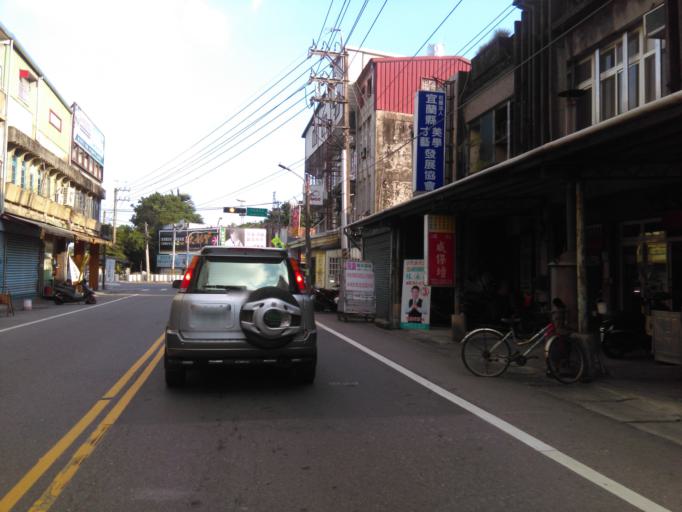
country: TW
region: Taiwan
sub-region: Yilan
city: Yilan
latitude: 24.7691
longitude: 121.7559
